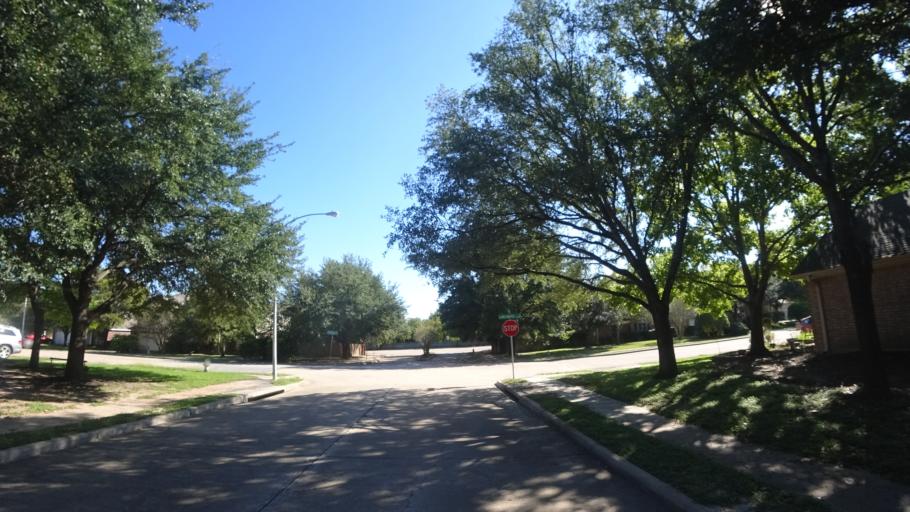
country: US
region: Texas
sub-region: Travis County
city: Manor
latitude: 30.3539
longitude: -97.6143
